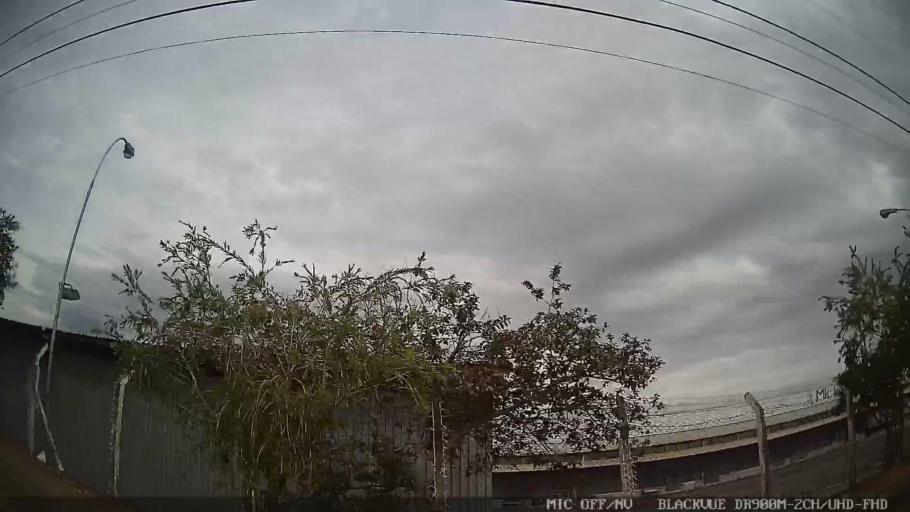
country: BR
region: Sao Paulo
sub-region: Salto
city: Salto
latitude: -23.1920
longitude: -47.2808
